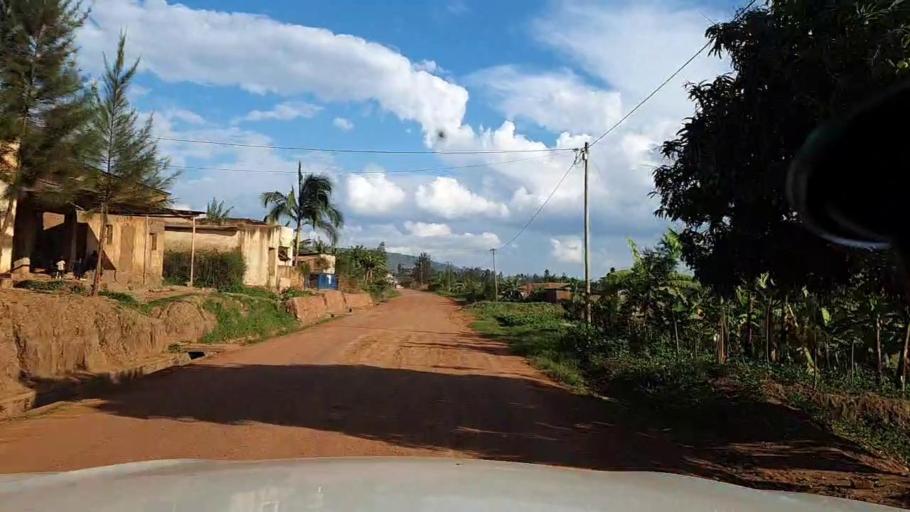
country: RW
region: Kigali
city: Kigali
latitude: -1.8925
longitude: 29.9591
